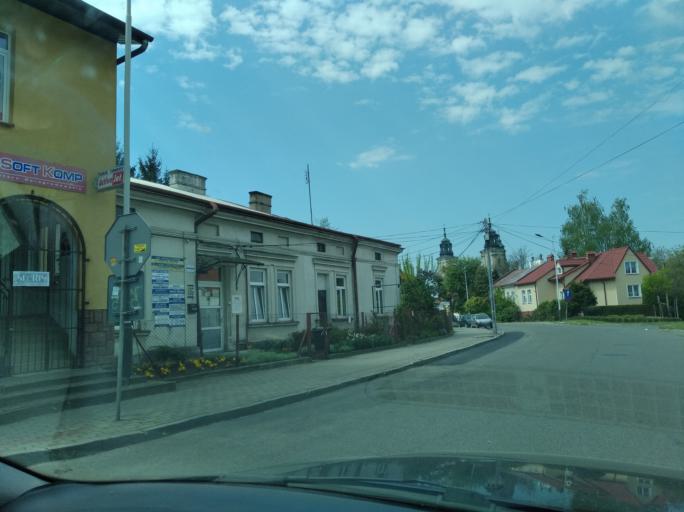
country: PL
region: Subcarpathian Voivodeship
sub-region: Powiat jaroslawski
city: Jaroslaw
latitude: 50.0177
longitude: 22.6680
